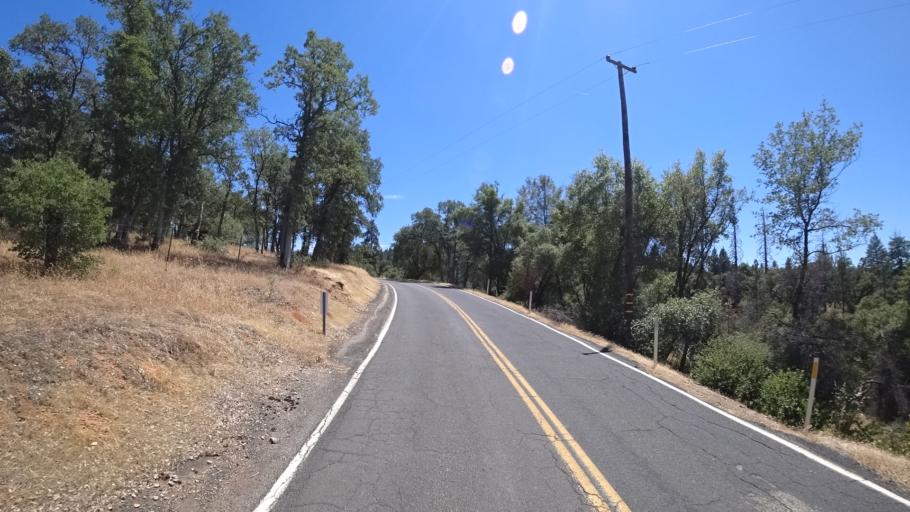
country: US
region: California
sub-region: Calaveras County
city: Forest Meadows
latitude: 38.2119
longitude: -120.4653
